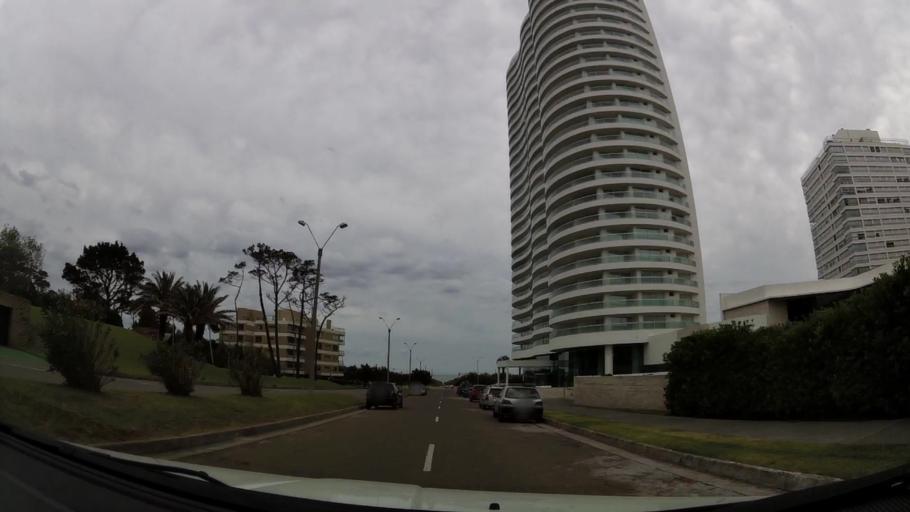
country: UY
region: Maldonado
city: Maldonado
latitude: -34.9272
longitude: -54.9599
